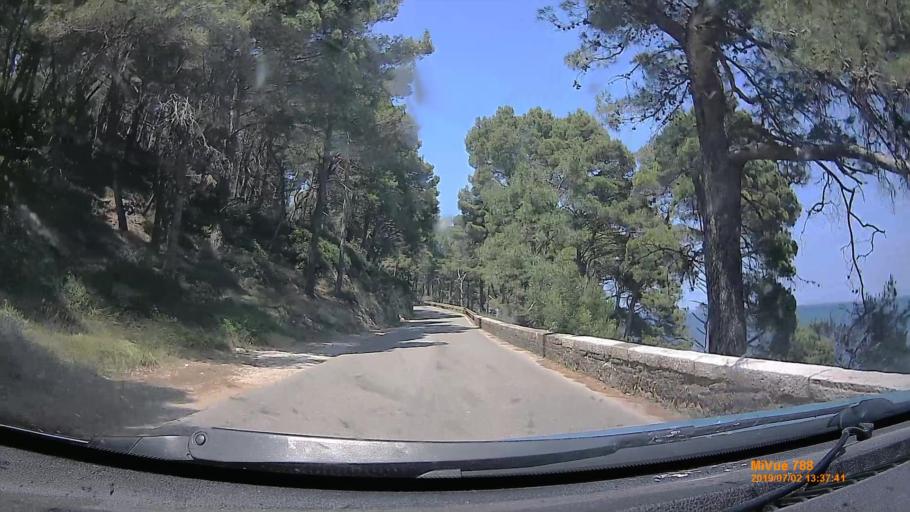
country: HR
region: Primorsko-Goranska
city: Mali Losinj
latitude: 44.5247
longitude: 14.4895
